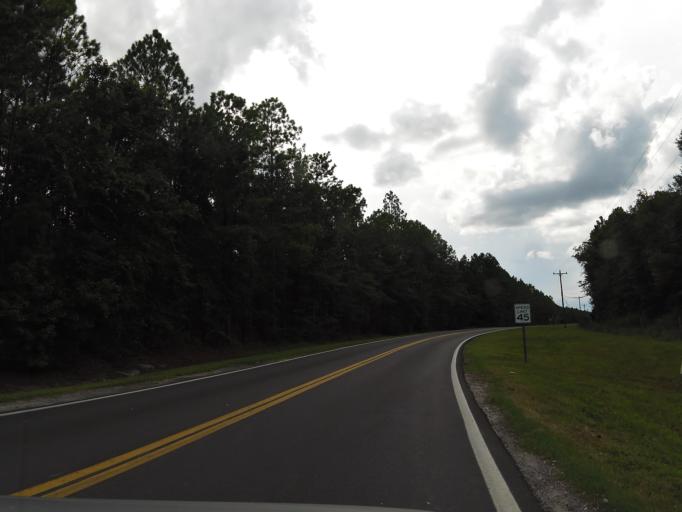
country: US
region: Florida
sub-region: Clay County
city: Green Cove Springs
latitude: 29.9940
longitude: -81.7315
